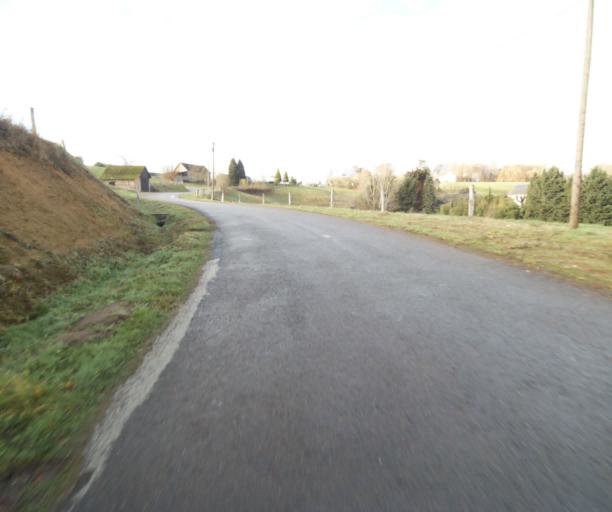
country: FR
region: Limousin
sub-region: Departement de la Correze
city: Saint-Mexant
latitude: 45.2425
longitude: 1.6353
